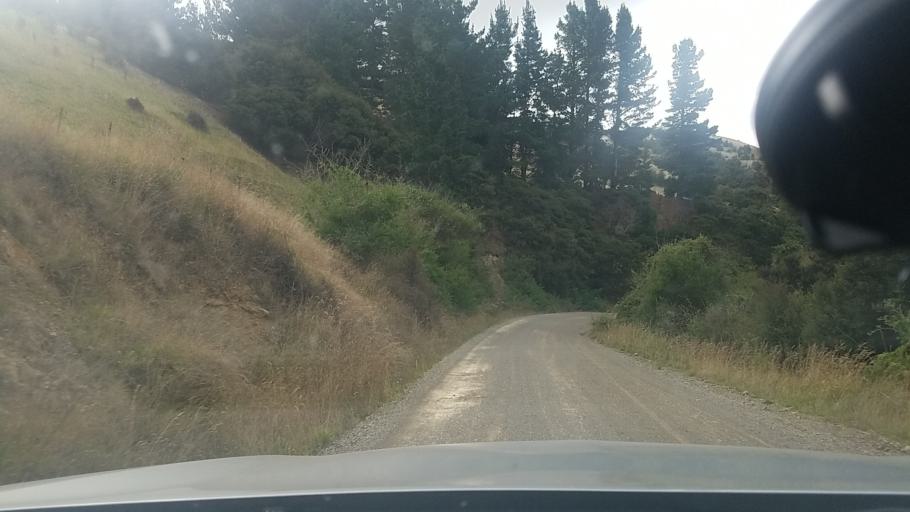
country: NZ
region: Marlborough
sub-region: Marlborough District
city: Blenheim
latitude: -41.5804
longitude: 174.0629
